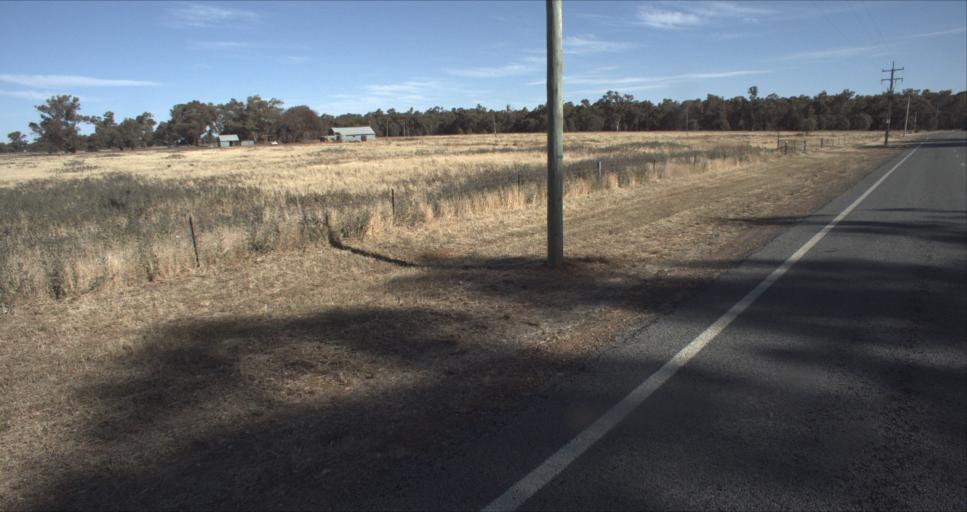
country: AU
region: New South Wales
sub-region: Leeton
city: Leeton
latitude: -34.6231
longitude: 146.3956
